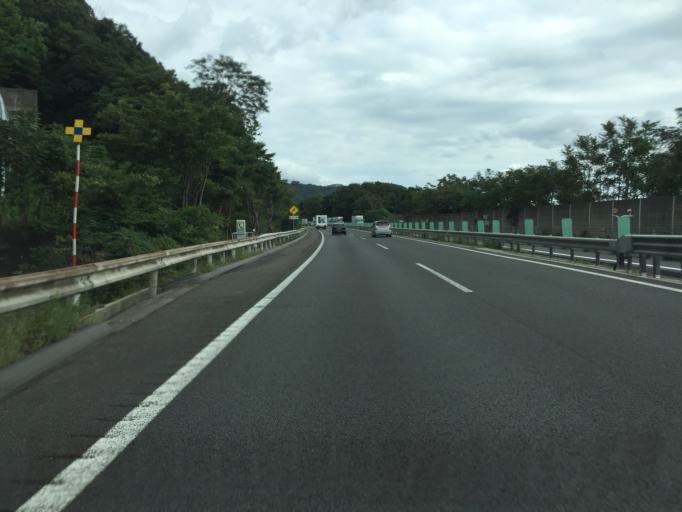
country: JP
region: Fukushima
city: Hobaramachi
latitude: 37.8836
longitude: 140.5395
